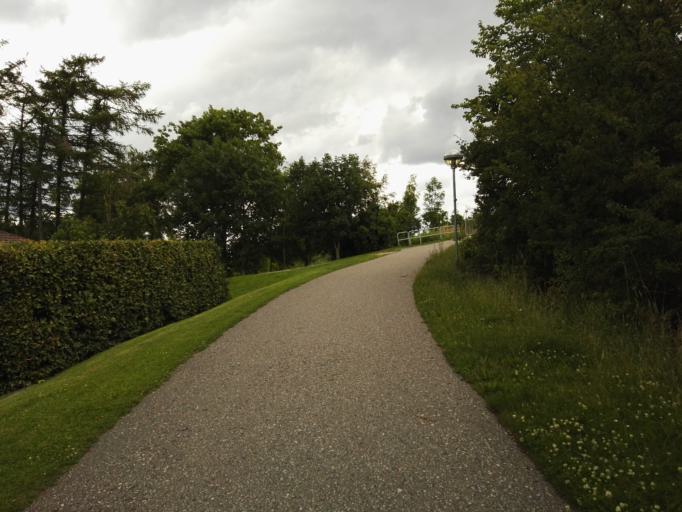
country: DK
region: Capital Region
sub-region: Egedal Kommune
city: Stenlose
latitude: 55.7630
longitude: 12.1910
